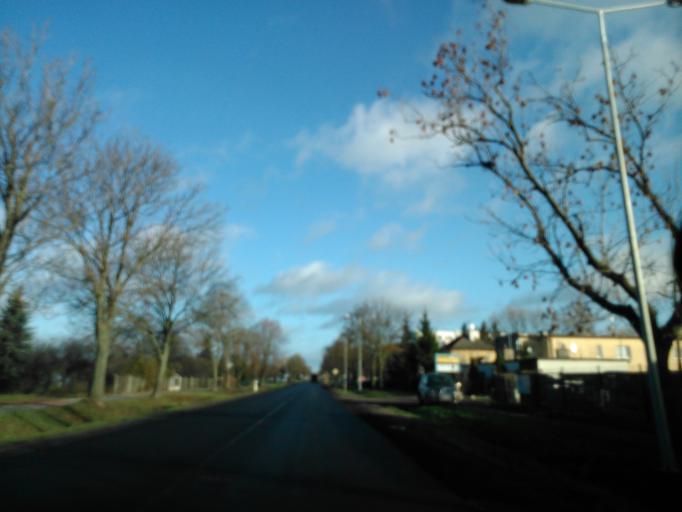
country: PL
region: Kujawsko-Pomorskie
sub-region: Powiat inowroclawski
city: Gniewkowo
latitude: 52.8888
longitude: 18.3964
